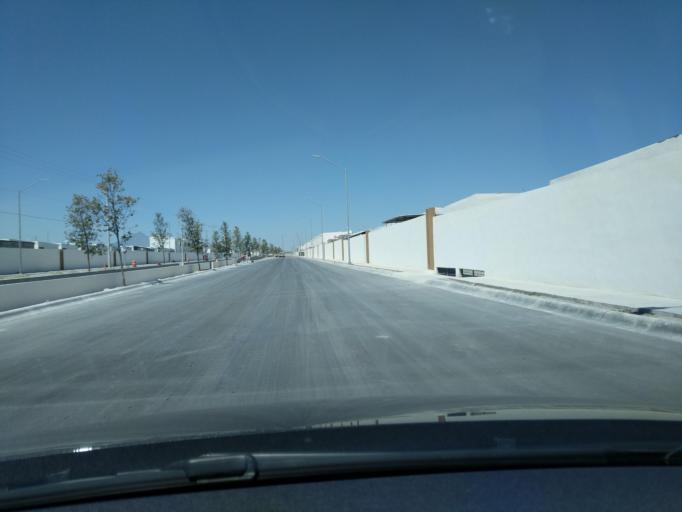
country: MX
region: Nuevo Leon
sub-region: Apodaca
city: Artemio Trevino
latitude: 25.8418
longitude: -100.1380
